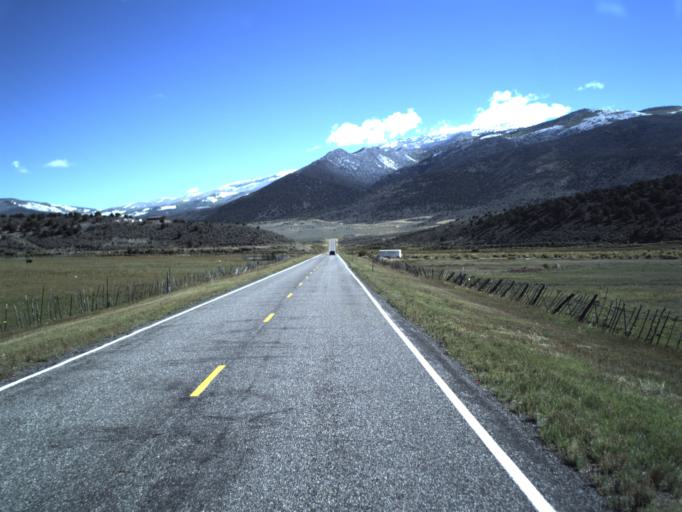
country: US
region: Utah
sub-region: Wayne County
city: Loa
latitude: 38.5593
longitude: -111.8581
